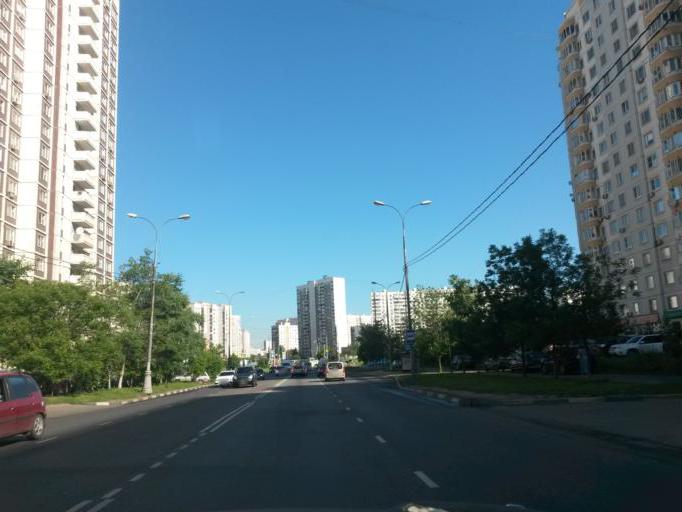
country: RU
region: Moscow
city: Lyublino
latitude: 55.6653
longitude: 37.7697
